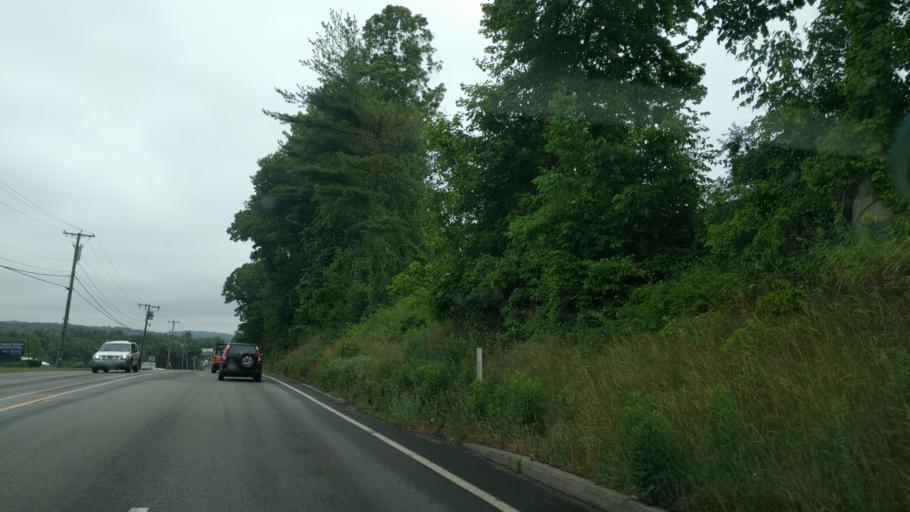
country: US
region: Massachusetts
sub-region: Worcester County
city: Auburn
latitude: 42.1984
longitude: -71.8186
